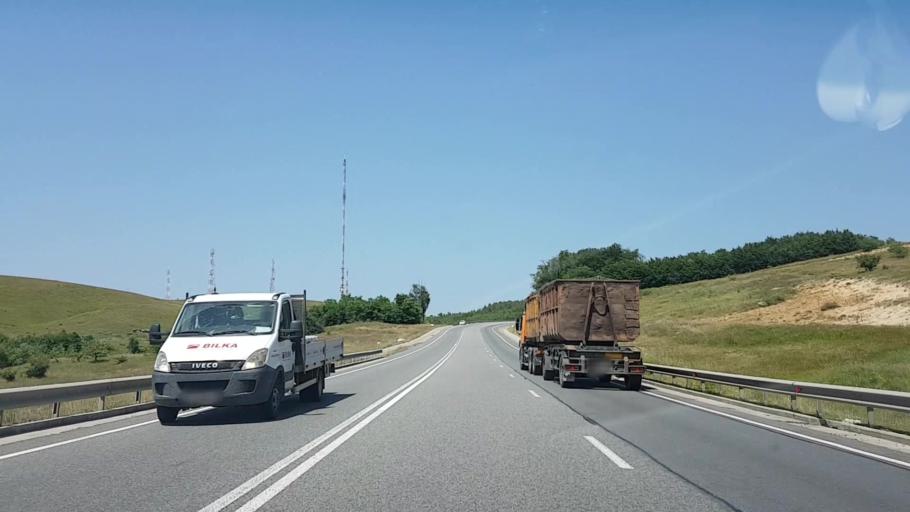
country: RO
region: Cluj
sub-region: Comuna Feleacu
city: Feleacu
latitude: 46.7036
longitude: 23.6423
